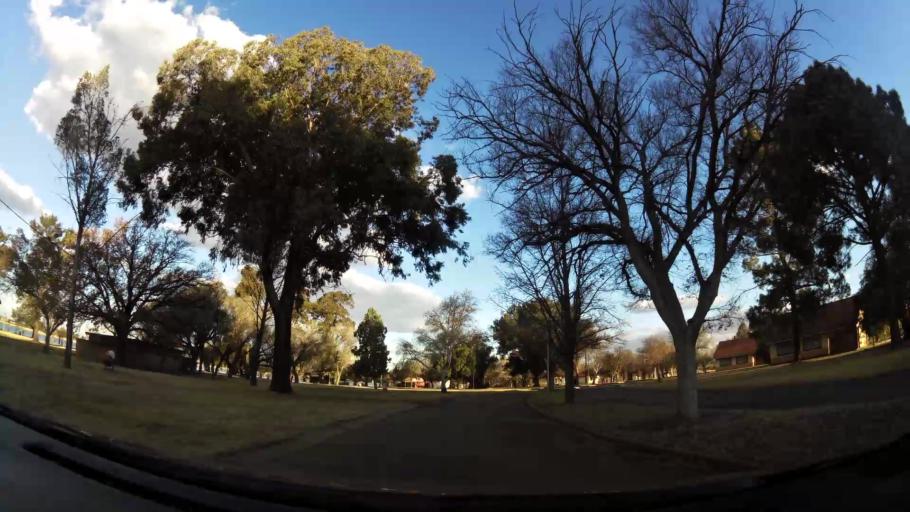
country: ZA
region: North-West
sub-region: Dr Kenneth Kaunda District Municipality
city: Potchefstroom
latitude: -26.6693
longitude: 27.0926
